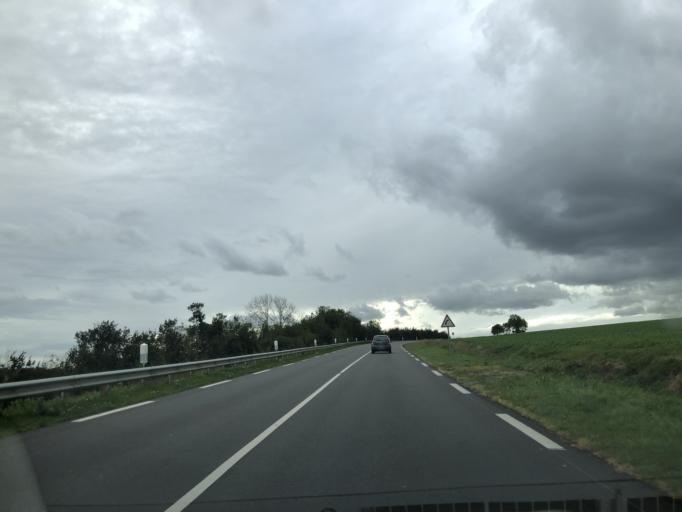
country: FR
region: Picardie
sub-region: Departement de la Somme
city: Abbeville
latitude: 50.1028
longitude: 1.7608
